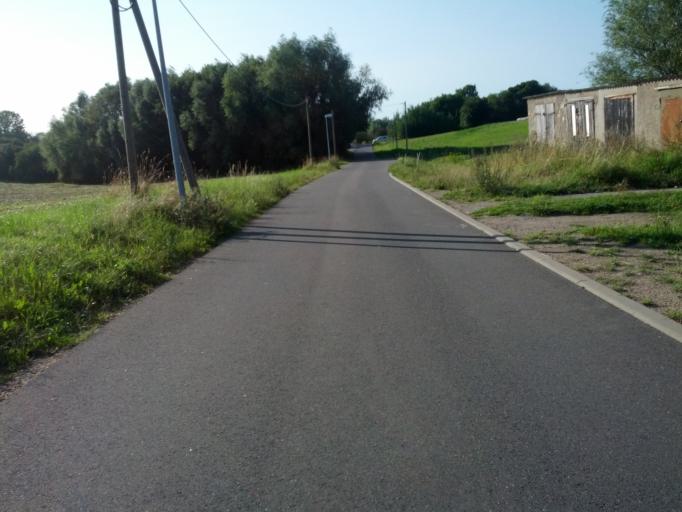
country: DE
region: Mecklenburg-Vorpommern
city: Bastorf
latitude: 54.1322
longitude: 11.6807
